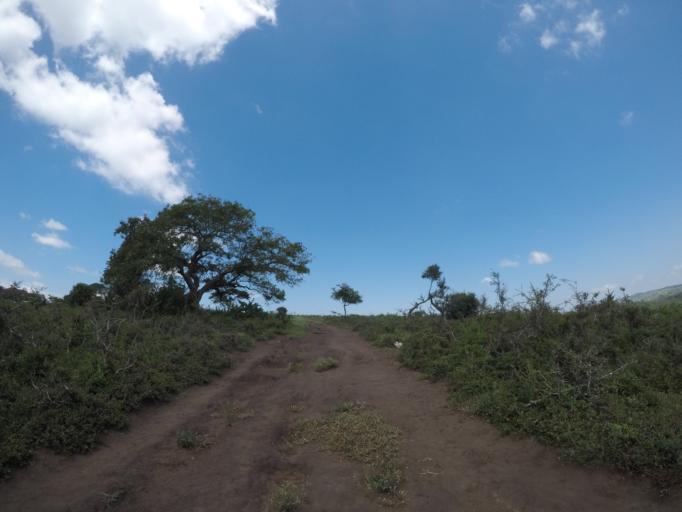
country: ZA
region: KwaZulu-Natal
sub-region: uThungulu District Municipality
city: Empangeni
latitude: -28.6025
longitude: 31.7342
